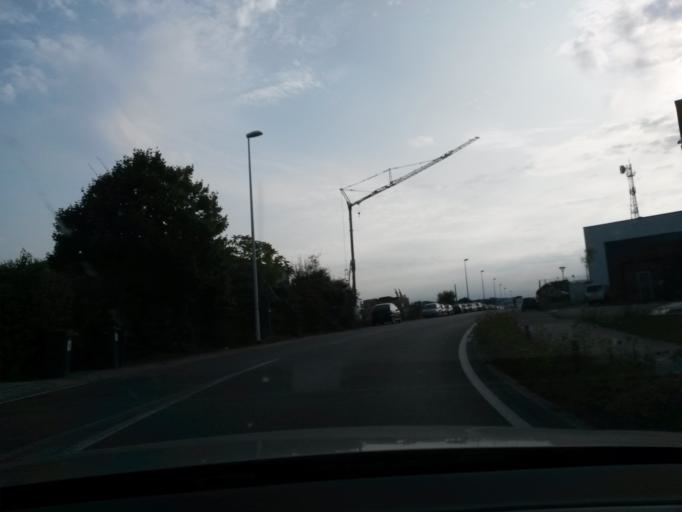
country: FR
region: Pays de la Loire
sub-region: Departement de la Loire-Atlantique
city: Guerande
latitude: 47.3253
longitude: -2.4102
